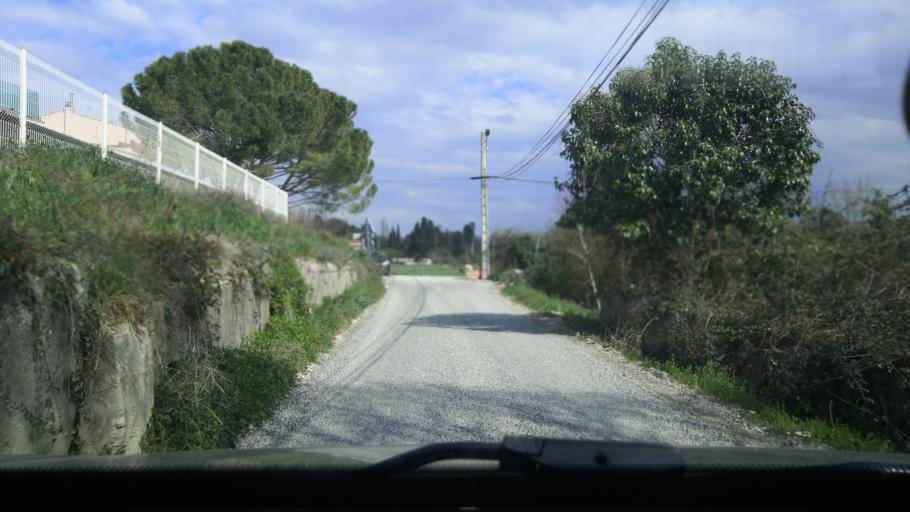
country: FR
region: Rhone-Alpes
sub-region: Departement de la Drome
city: Montelimar
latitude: 44.5664
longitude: 4.7714
